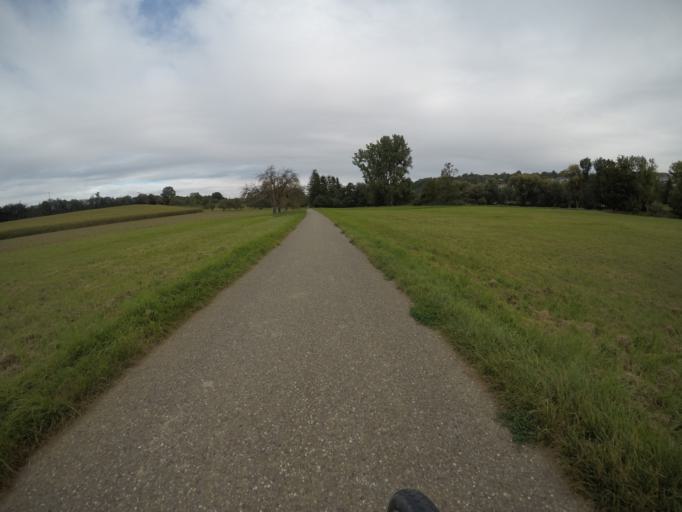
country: DE
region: Baden-Wuerttemberg
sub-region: Regierungsbezirk Stuttgart
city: Erdmannhausen
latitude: 48.8827
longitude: 9.2748
